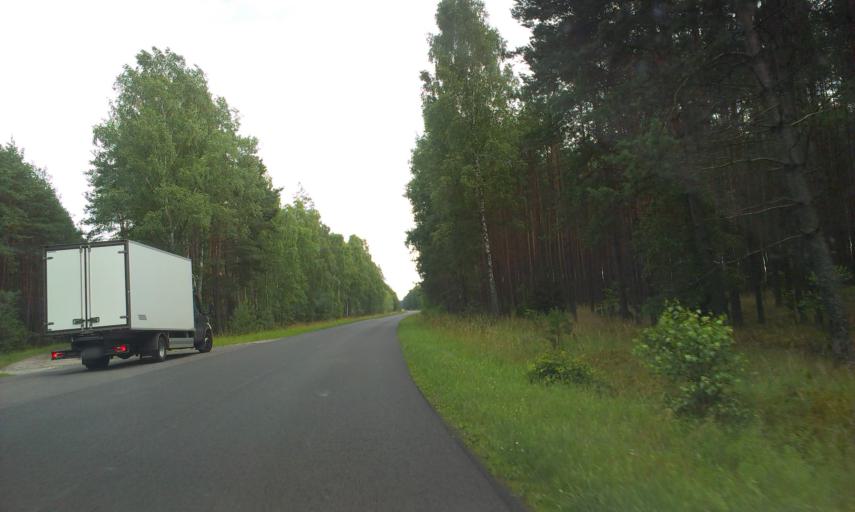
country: PL
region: Greater Poland Voivodeship
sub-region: Powiat zlotowski
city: Okonek
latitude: 53.5279
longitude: 16.9594
